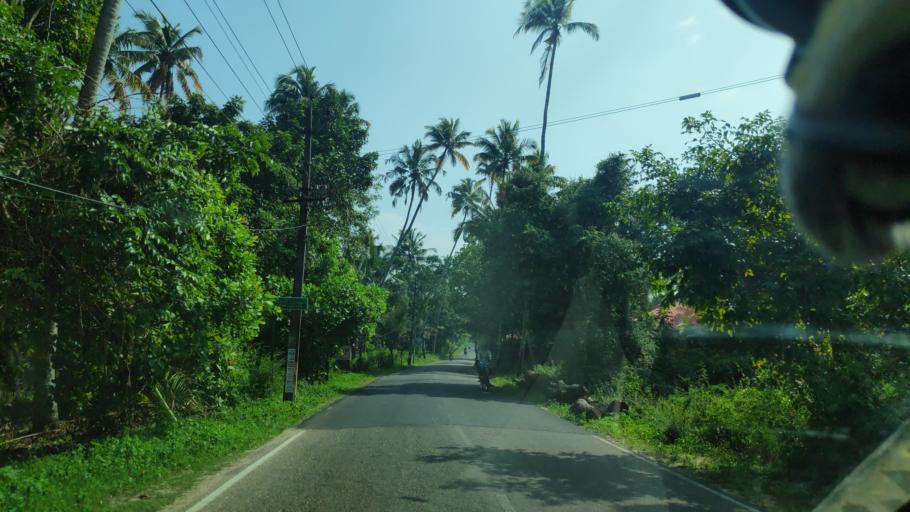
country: IN
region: Kerala
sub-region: Alappuzha
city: Shertallai
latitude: 9.6262
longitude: 76.3001
